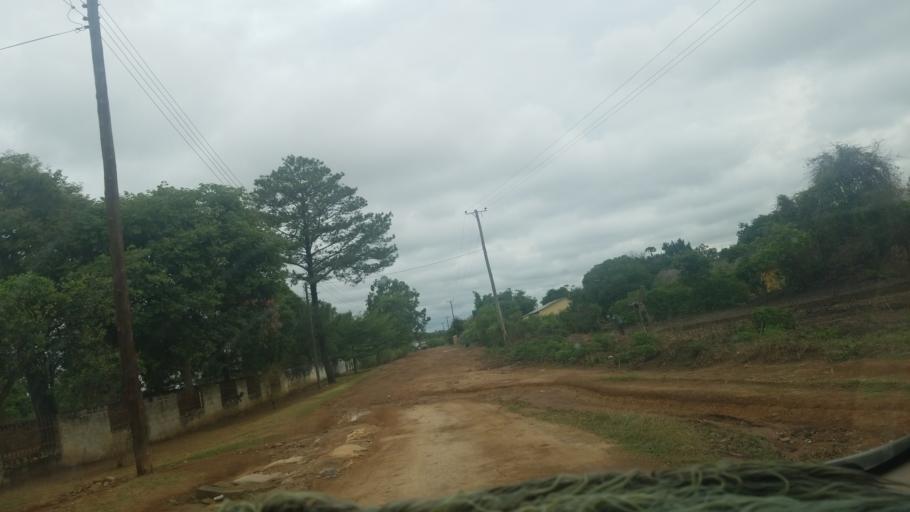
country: ZM
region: Luapula
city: Mansa
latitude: -11.1953
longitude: 28.8985
